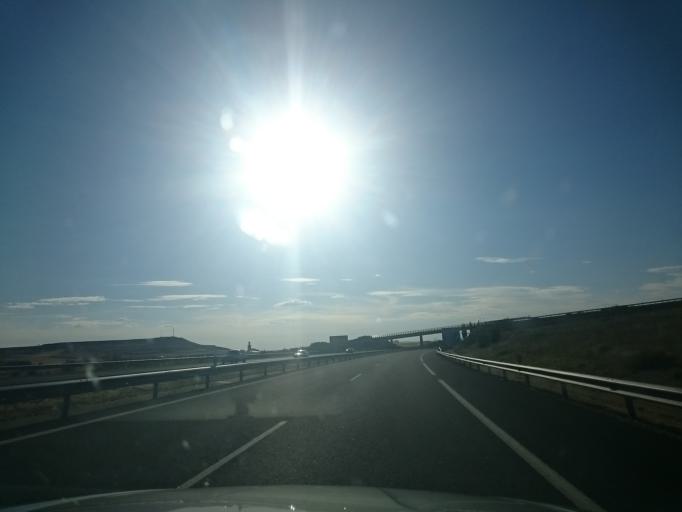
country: ES
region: Castille and Leon
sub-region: Provincia de Burgos
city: Sasamon
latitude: 42.3952
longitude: -4.0208
